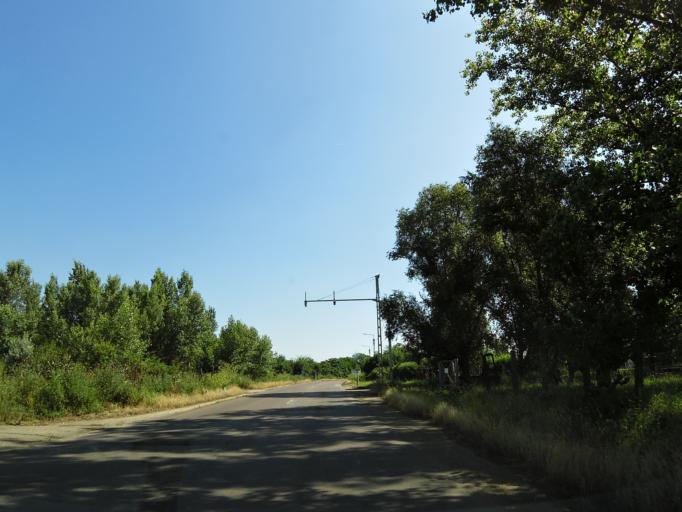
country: HU
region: Jasz-Nagykun-Szolnok
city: Toszeg
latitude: 47.1321
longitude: 20.1439
